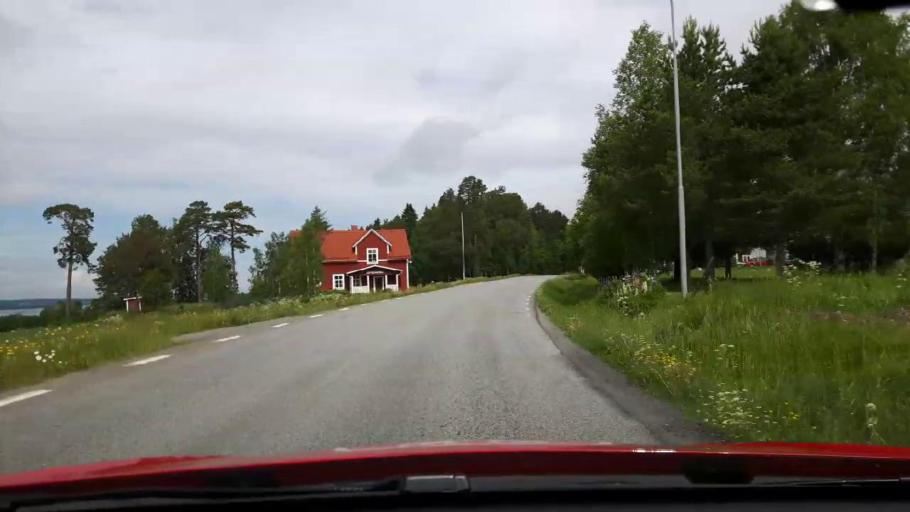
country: SE
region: Jaemtland
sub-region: OEstersunds Kommun
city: Ostersund
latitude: 63.0478
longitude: 14.4523
